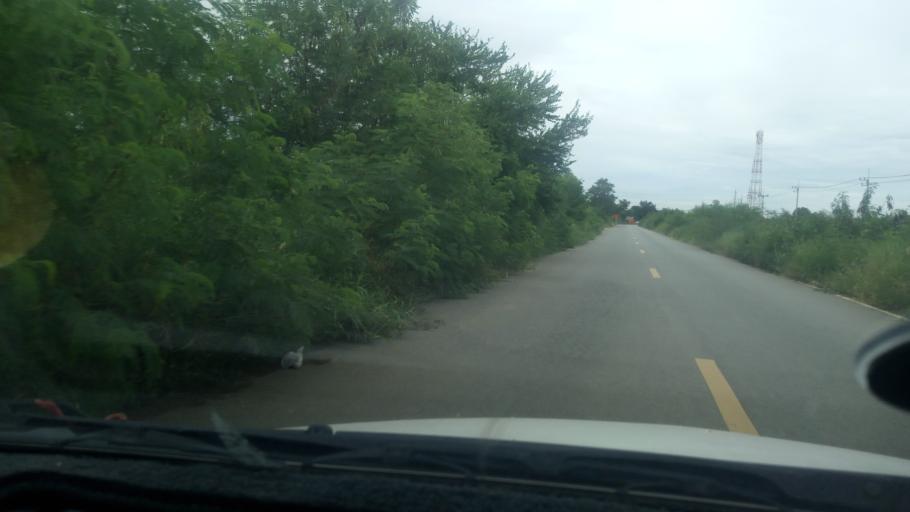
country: TH
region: Chon Buri
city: Phan Thong
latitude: 13.5283
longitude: 101.1554
